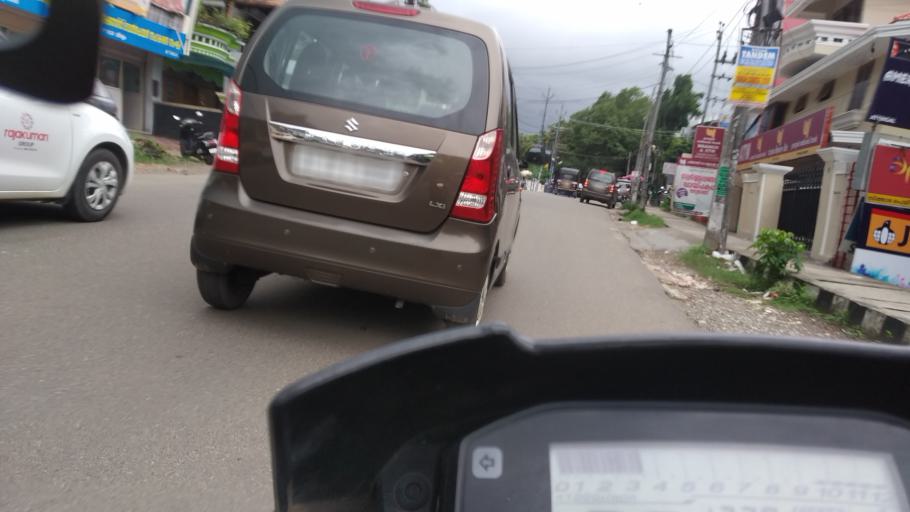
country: IN
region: Kerala
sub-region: Thiruvananthapuram
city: Attingal
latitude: 8.6954
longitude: 76.8127
